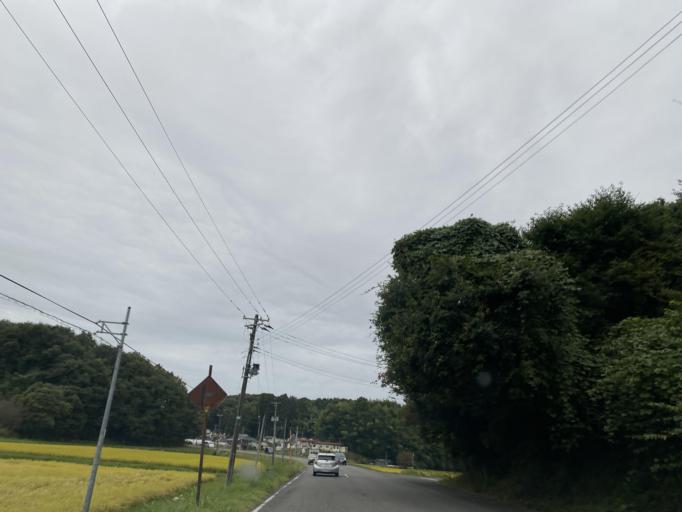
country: JP
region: Fukushima
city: Sukagawa
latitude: 37.3040
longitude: 140.2553
